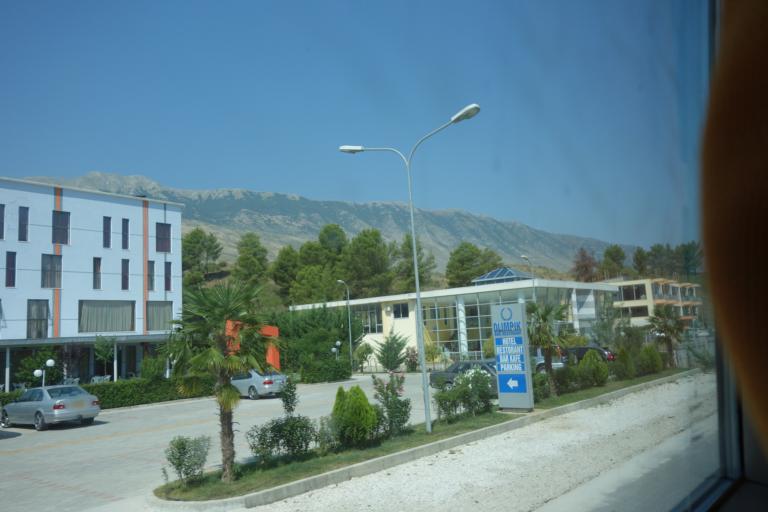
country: AL
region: Gjirokaster
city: Gjirokaster
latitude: 40.0996
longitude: 20.1294
